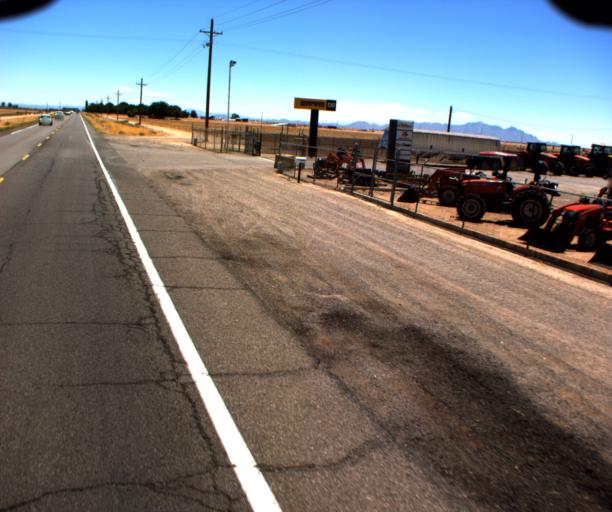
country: US
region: Arizona
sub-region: Pinal County
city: Casa Grande
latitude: 32.8797
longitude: -111.6631
